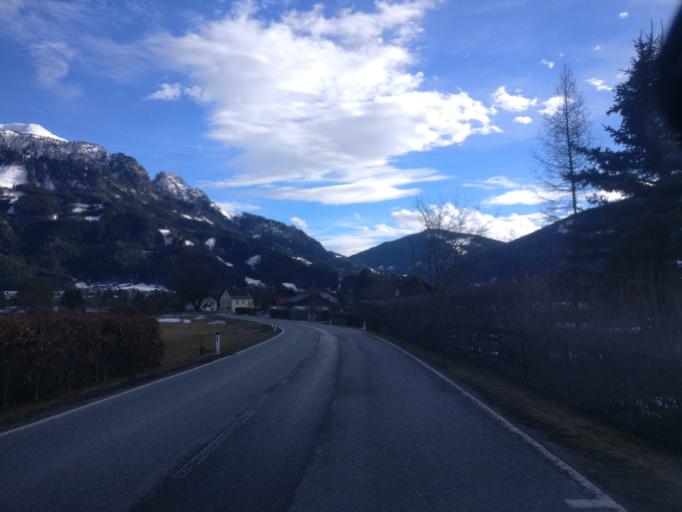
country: AT
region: Styria
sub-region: Politischer Bezirk Liezen
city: Hall bei Admont
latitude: 47.5895
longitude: 14.4698
